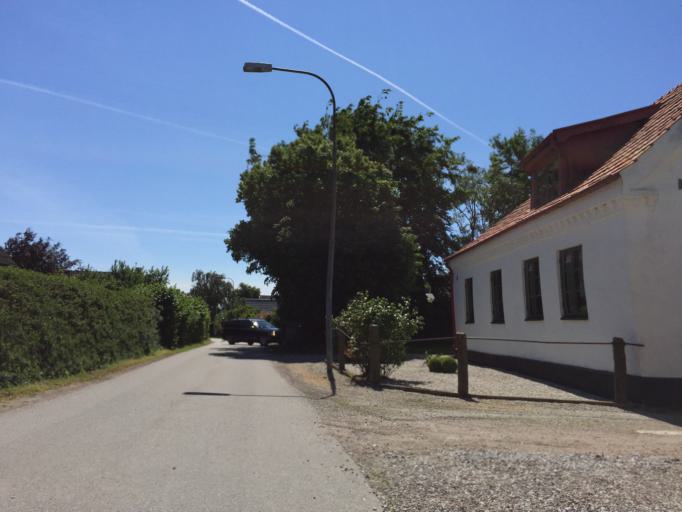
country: SE
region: Skane
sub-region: Trelleborgs Kommun
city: Skare
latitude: 55.3756
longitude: 13.0824
